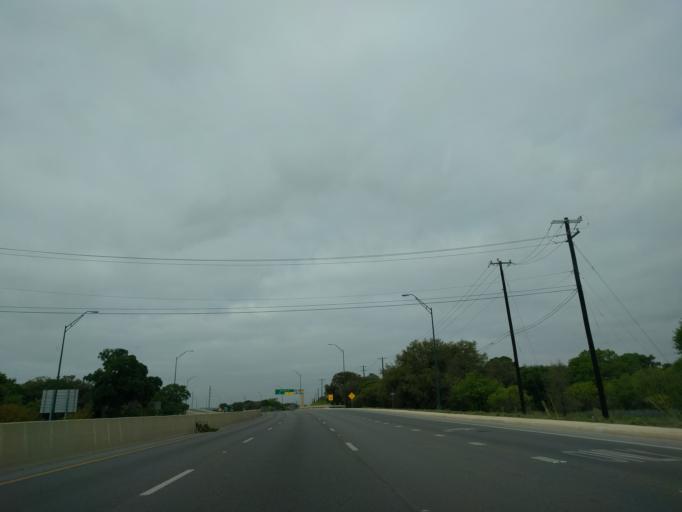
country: US
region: Texas
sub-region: Bexar County
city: Alamo Heights
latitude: 29.5471
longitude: -98.4485
